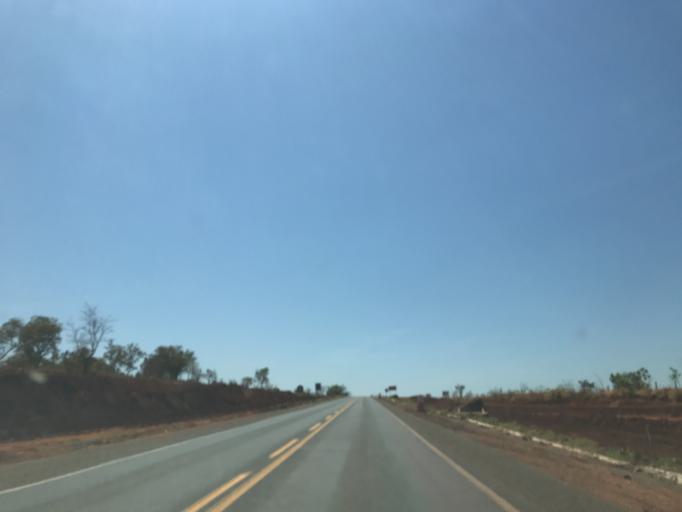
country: BR
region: Minas Gerais
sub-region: Prata
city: Prata
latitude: -19.4348
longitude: -48.8889
